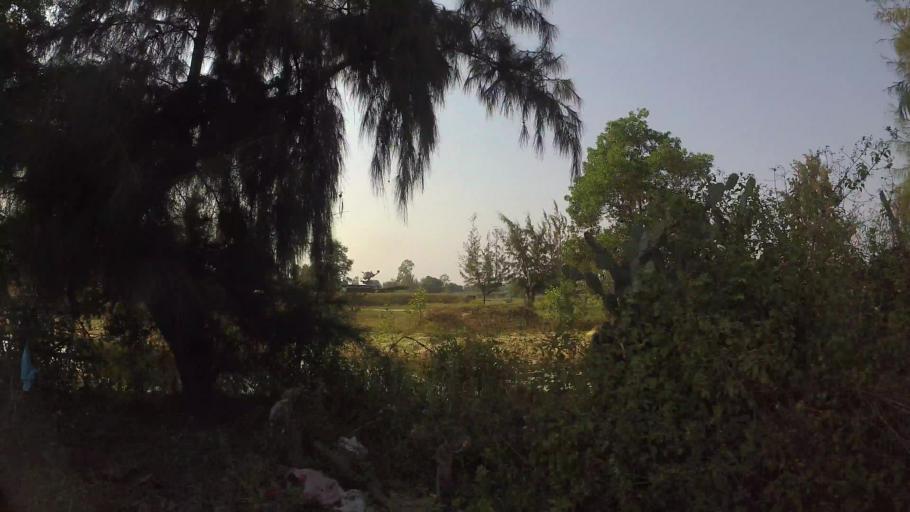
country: VN
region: Da Nang
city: Ngu Hanh Son
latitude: 15.9553
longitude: 108.2610
